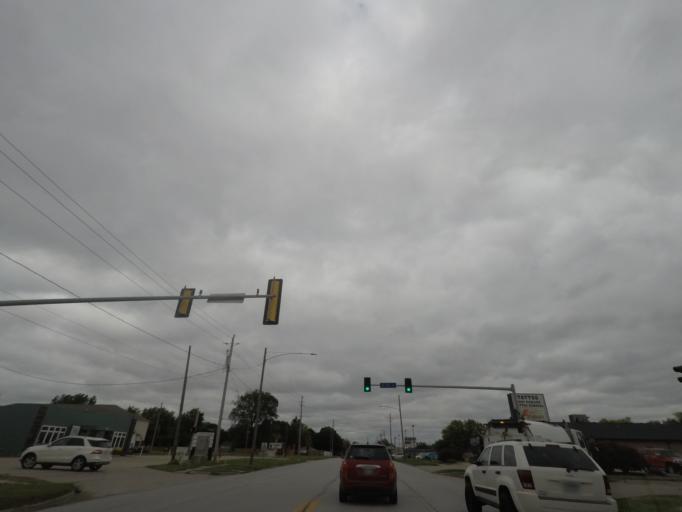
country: US
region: Iowa
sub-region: Polk County
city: Ankeny
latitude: 41.7232
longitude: -93.6004
